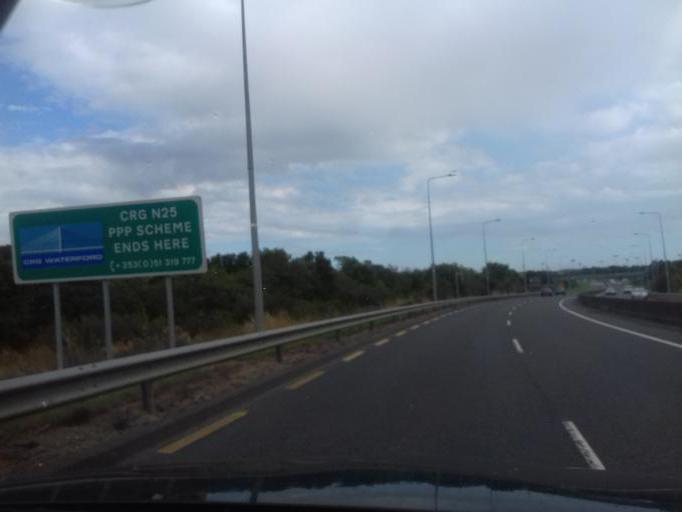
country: IE
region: Munster
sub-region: Waterford
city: Waterford
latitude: 52.2585
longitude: -7.1816
